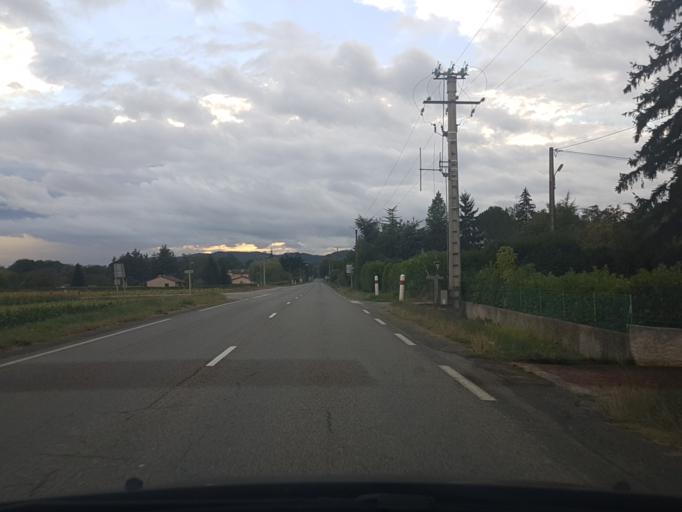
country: FR
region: Midi-Pyrenees
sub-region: Departement de l'Ariege
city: Mirepoix
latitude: 43.0960
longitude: 1.8848
